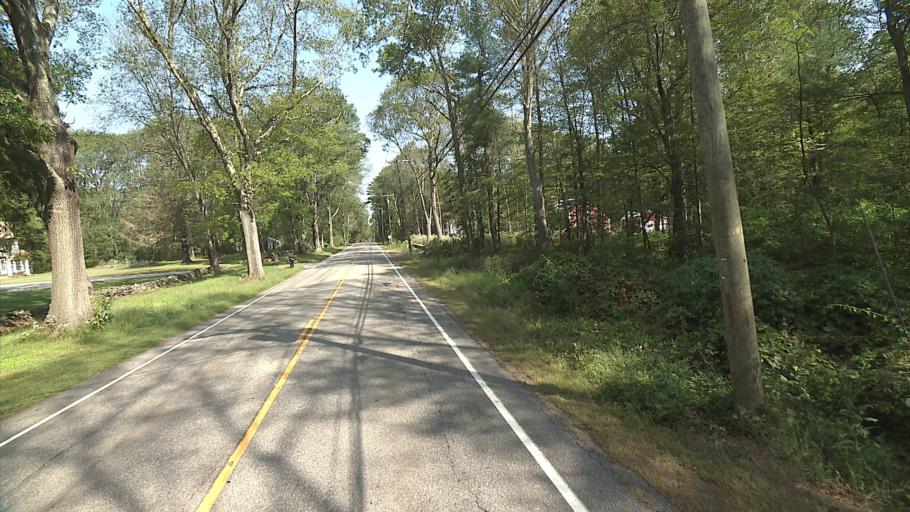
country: US
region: Connecticut
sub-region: Windham County
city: East Brooklyn
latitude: 41.8445
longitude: -71.9588
